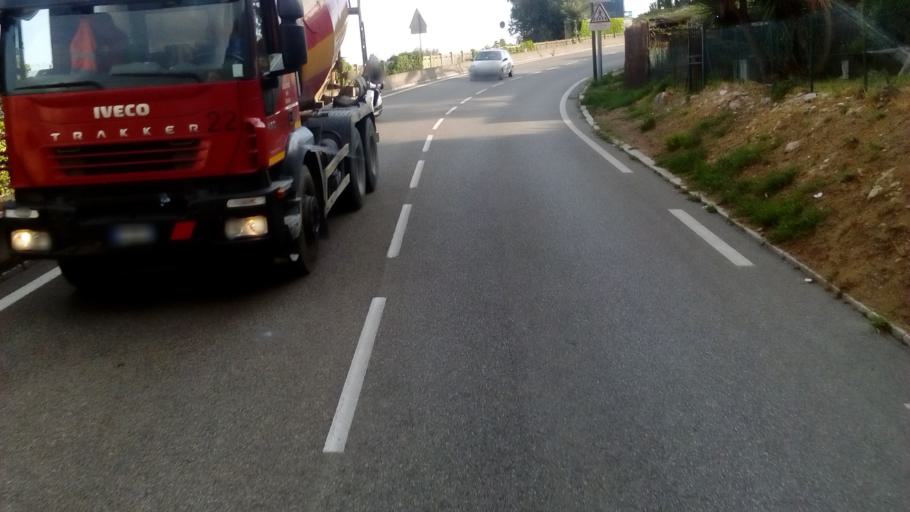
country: MC
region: Commune de Monaco
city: Saint-Roman
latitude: 43.7527
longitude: 7.4321
